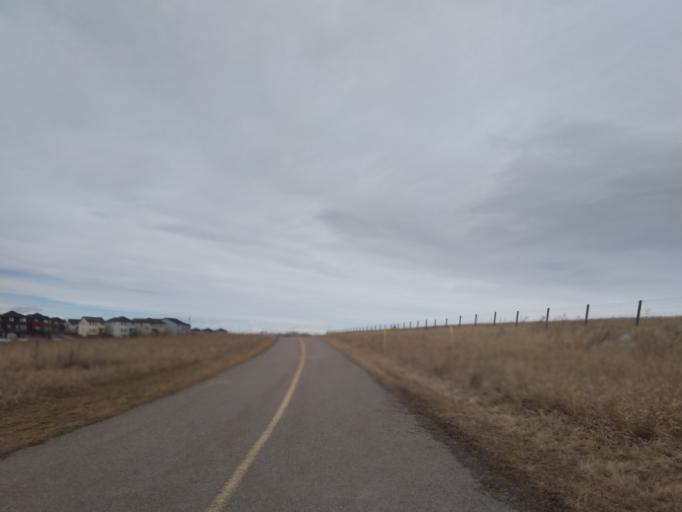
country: CA
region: Alberta
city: Chestermere
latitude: 51.1334
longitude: -113.9236
